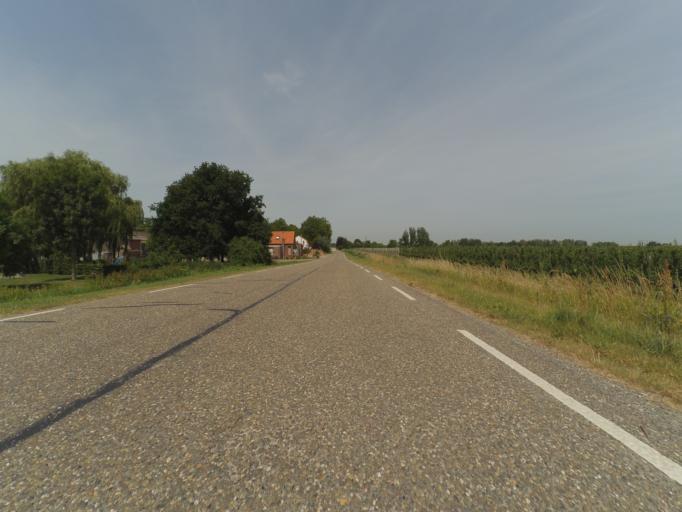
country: NL
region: North Brabant
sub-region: Gemeente Steenbergen
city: Nieuw-Vossemeer
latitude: 51.5754
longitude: 4.1950
